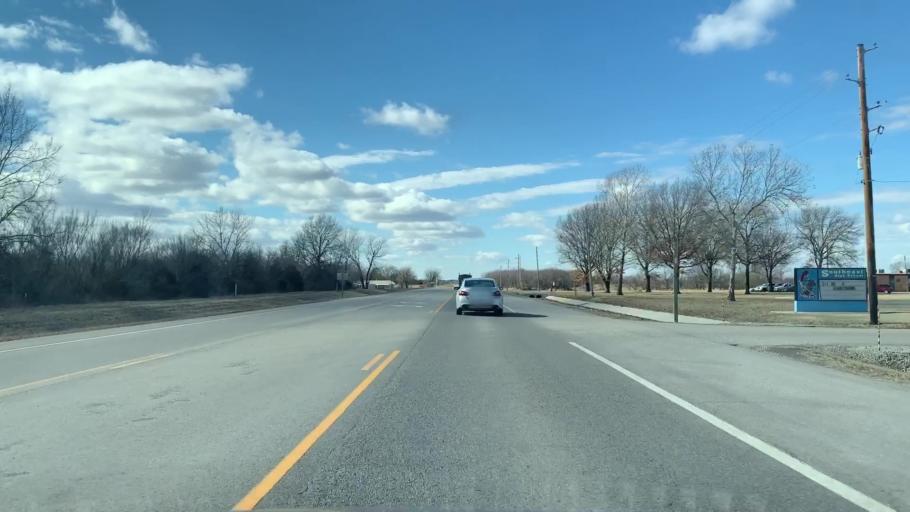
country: US
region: Kansas
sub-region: Crawford County
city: Pittsburg
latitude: 37.3395
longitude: -94.8356
